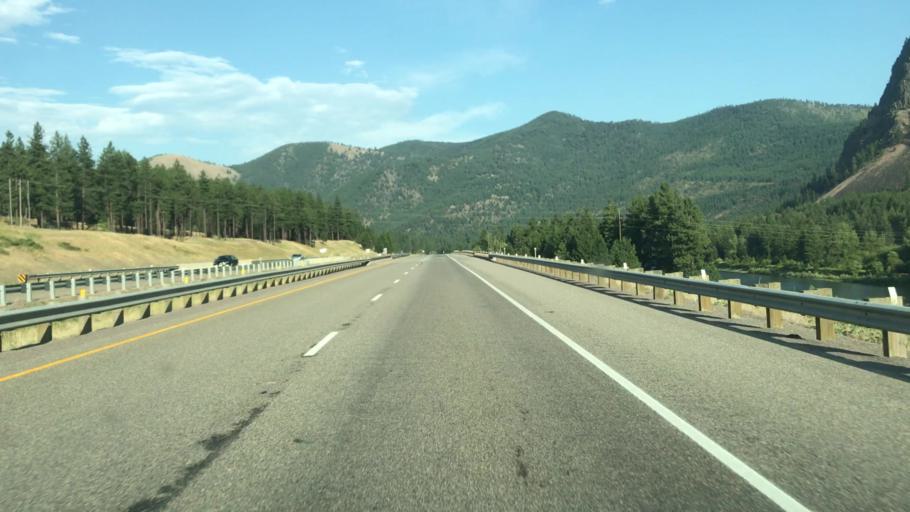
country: US
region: Montana
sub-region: Missoula County
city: Frenchtown
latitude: 46.9936
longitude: -114.4469
